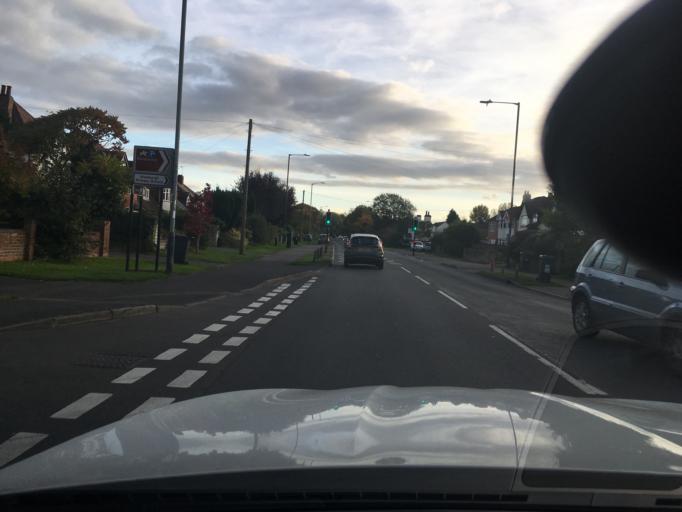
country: GB
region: England
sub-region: Warwickshire
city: Warwick
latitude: 52.2728
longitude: -1.5967
